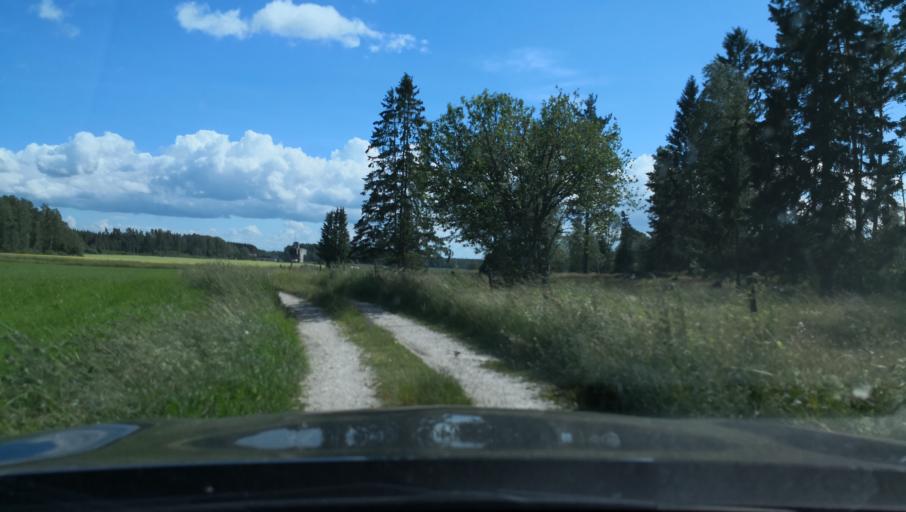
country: SE
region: Vaestmanland
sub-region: Kungsors Kommun
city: Kungsoer
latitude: 59.3285
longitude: 16.0652
